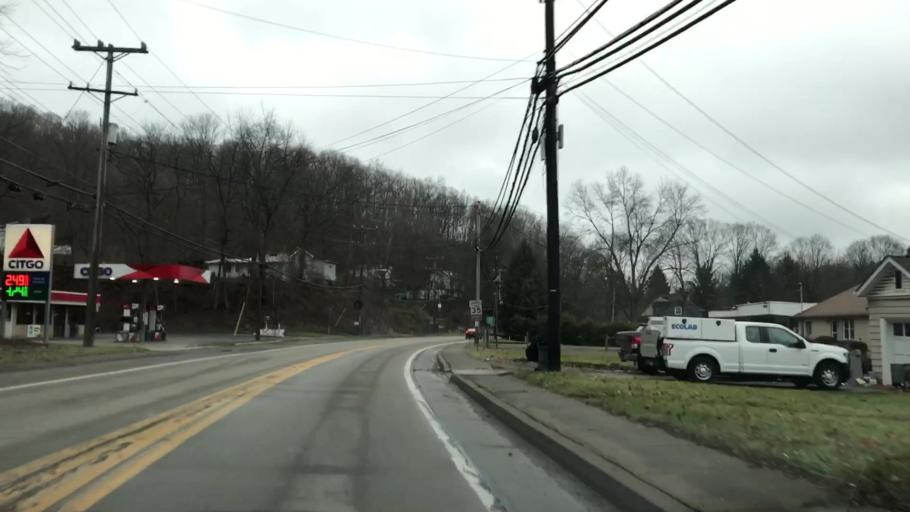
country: US
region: Pennsylvania
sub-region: Allegheny County
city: Leetsdale
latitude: 40.5448
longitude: -80.2181
